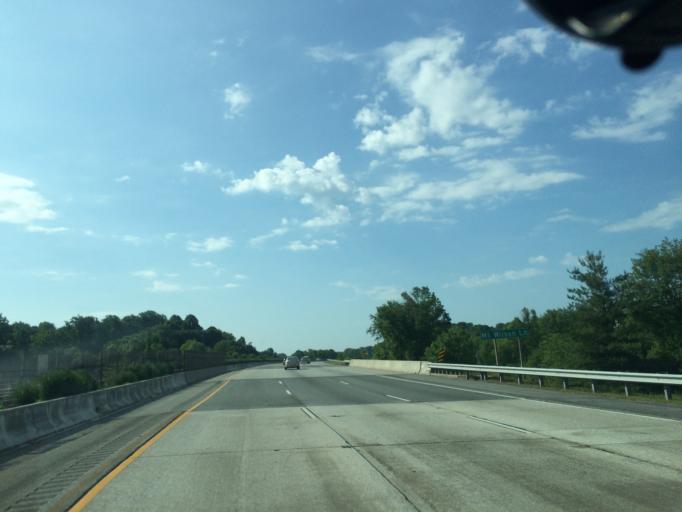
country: US
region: Maryland
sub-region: Baltimore County
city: Garrison
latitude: 39.3843
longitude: -76.7563
